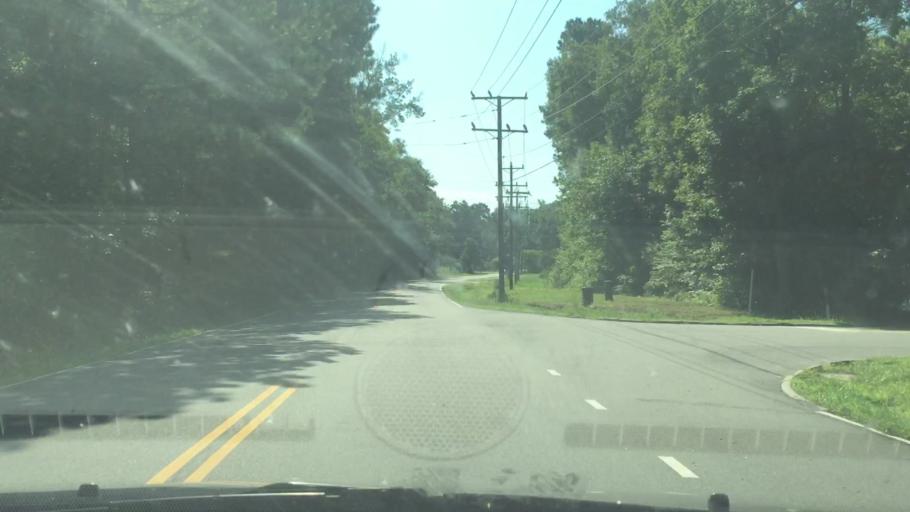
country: US
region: Virginia
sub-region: Hanover County
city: Ashland
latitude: 37.7420
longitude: -77.4641
